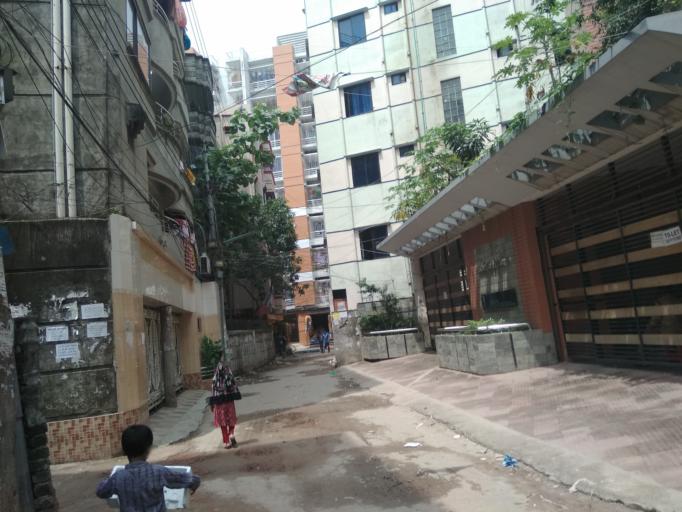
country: BD
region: Dhaka
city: Azimpur
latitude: 23.8030
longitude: 90.3663
